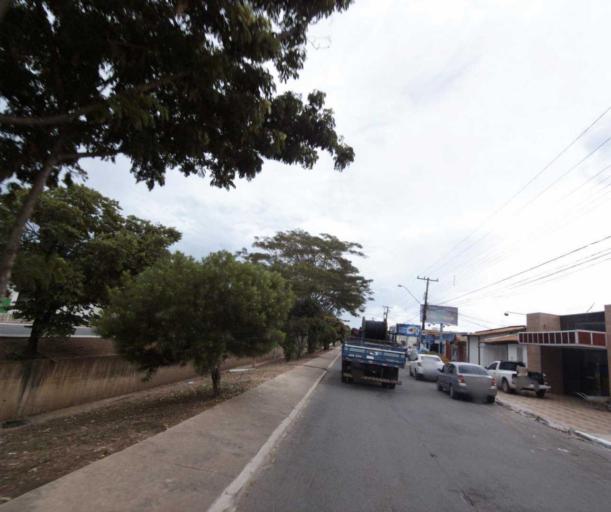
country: BR
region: Mato Grosso
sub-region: Cuiaba
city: Cuiaba
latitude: -15.6162
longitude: -56.0761
